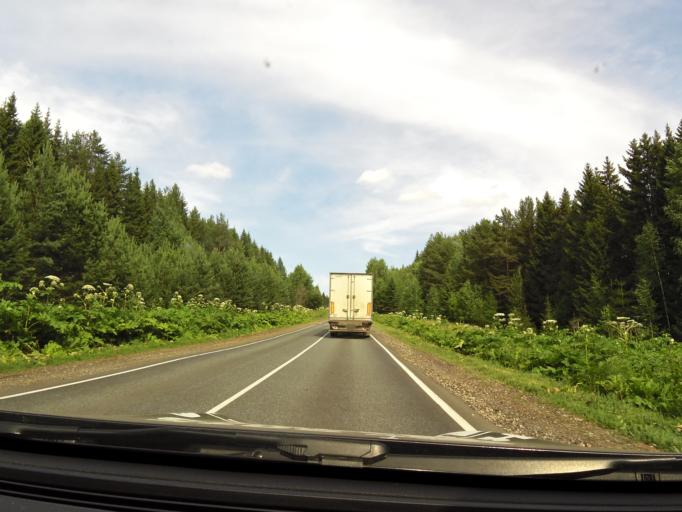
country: RU
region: Kirov
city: Slobodskoy
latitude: 58.7650
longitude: 50.3472
